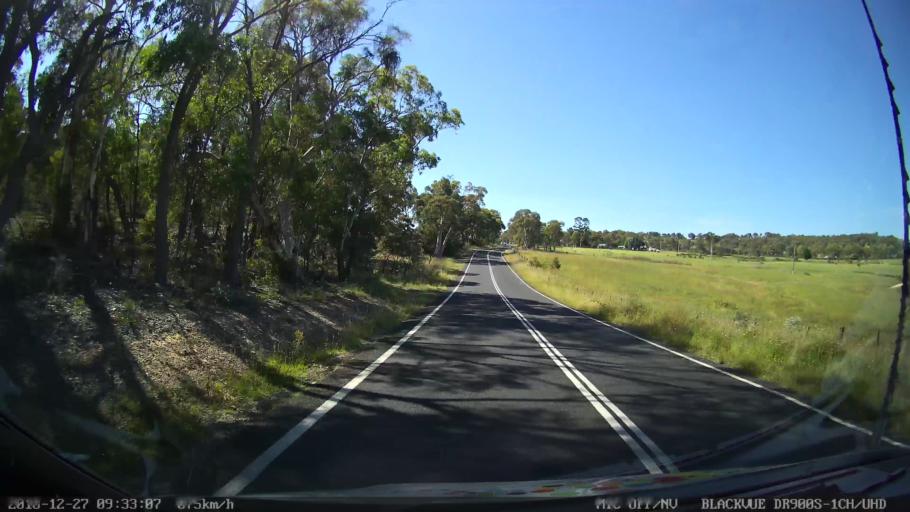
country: AU
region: New South Wales
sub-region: Lithgow
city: Portland
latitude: -33.2153
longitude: 150.0199
